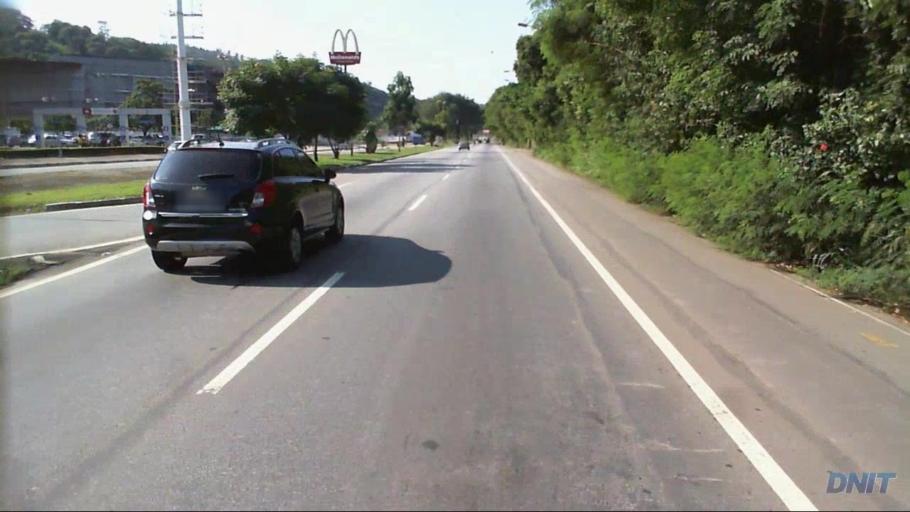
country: BR
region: Minas Gerais
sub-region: Ipatinga
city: Ipatinga
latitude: -19.4991
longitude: -42.5659
